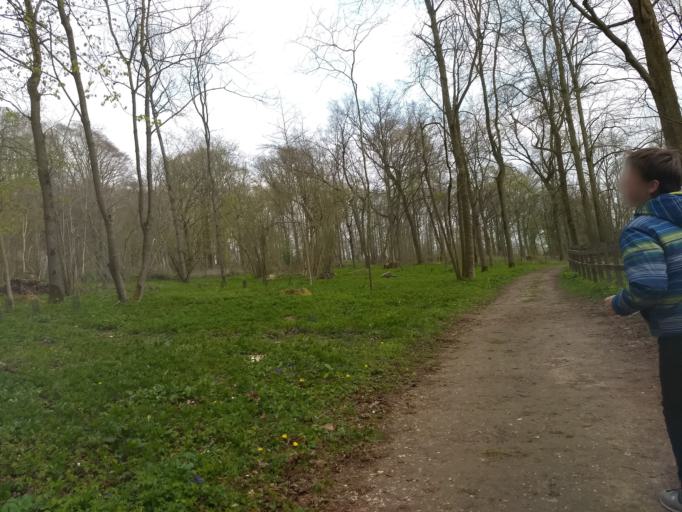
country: FR
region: Nord-Pas-de-Calais
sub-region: Departement du Pas-de-Calais
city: Maroeuil
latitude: 50.3315
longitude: 2.6953
